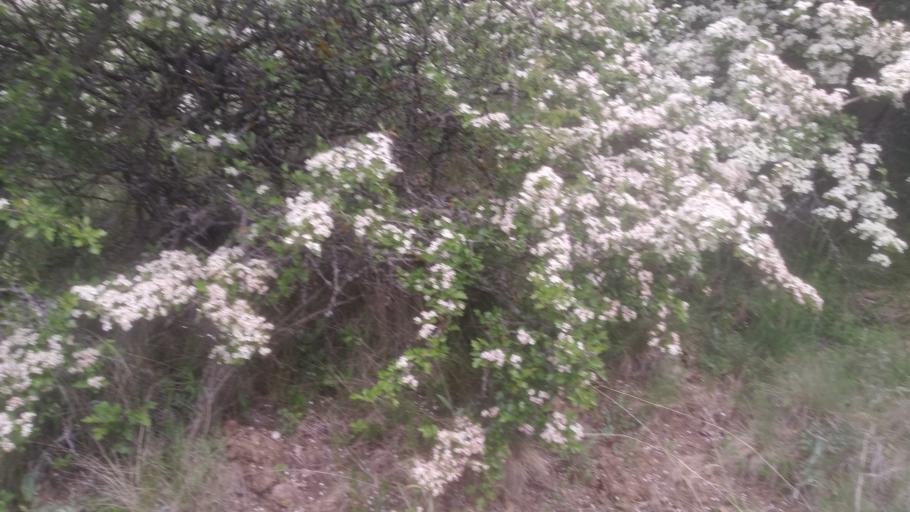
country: HU
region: Pest
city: Pilisborosjeno
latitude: 47.5551
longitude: 18.9758
